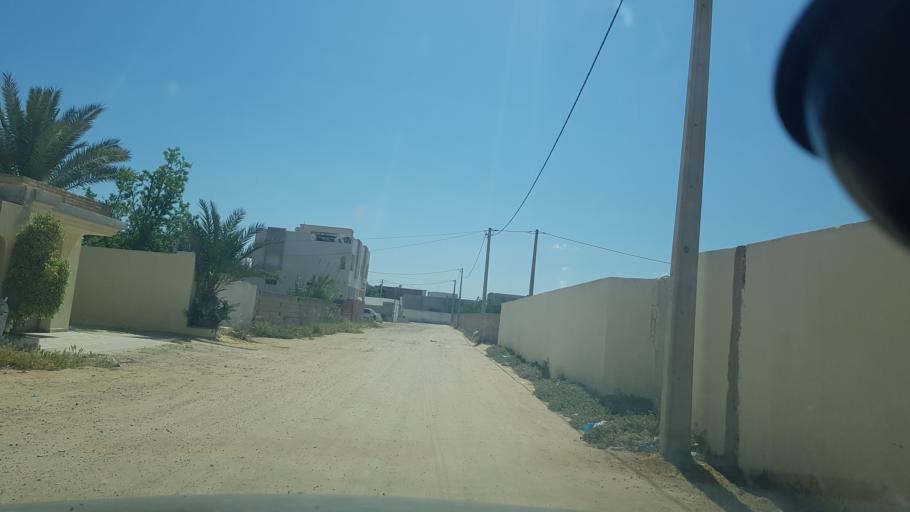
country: TN
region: Safaqis
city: Al Qarmadah
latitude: 34.8230
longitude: 10.7571
